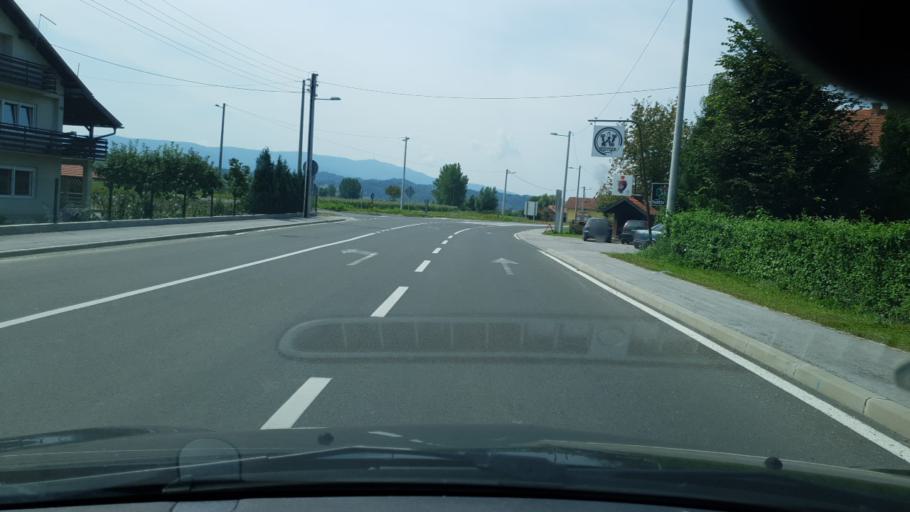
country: HR
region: Krapinsko-Zagorska
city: Bedekovcina
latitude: 46.0386
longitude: 15.9815
